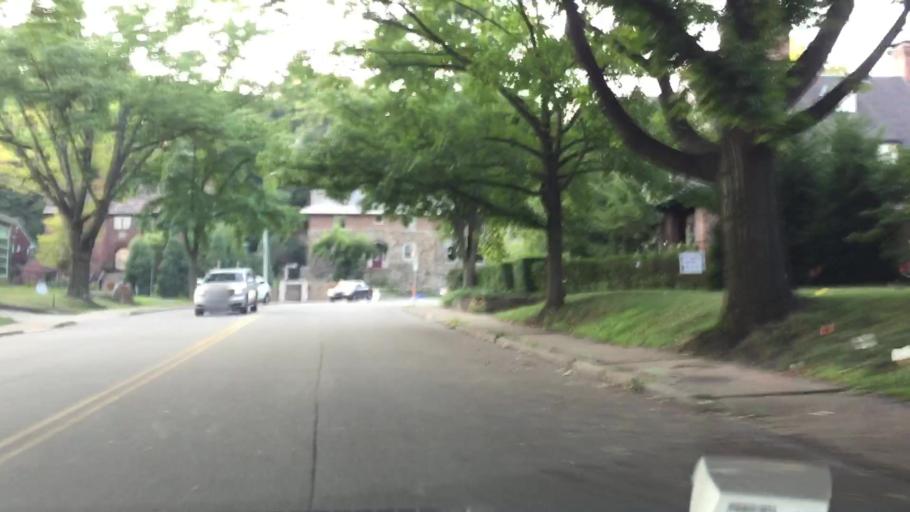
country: US
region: Pennsylvania
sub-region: Allegheny County
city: Bloomfield
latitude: 40.4487
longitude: -79.9550
